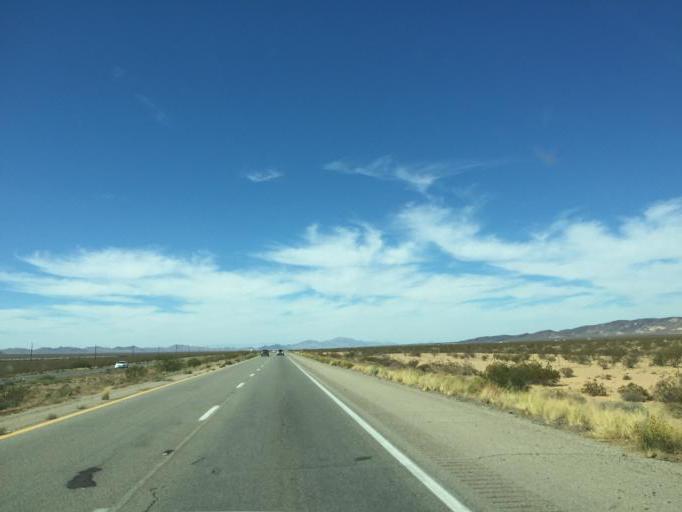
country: US
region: Arizona
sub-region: Mohave County
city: Dolan Springs
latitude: 35.5723
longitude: -114.3817
